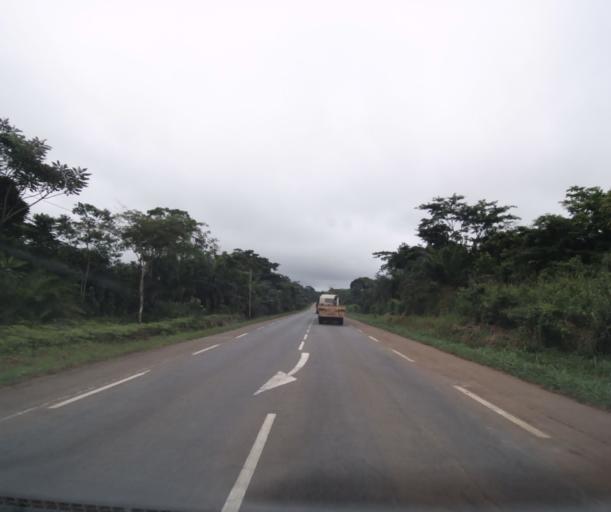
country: CM
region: Centre
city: Mbankomo
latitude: 3.7688
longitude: 11.1369
